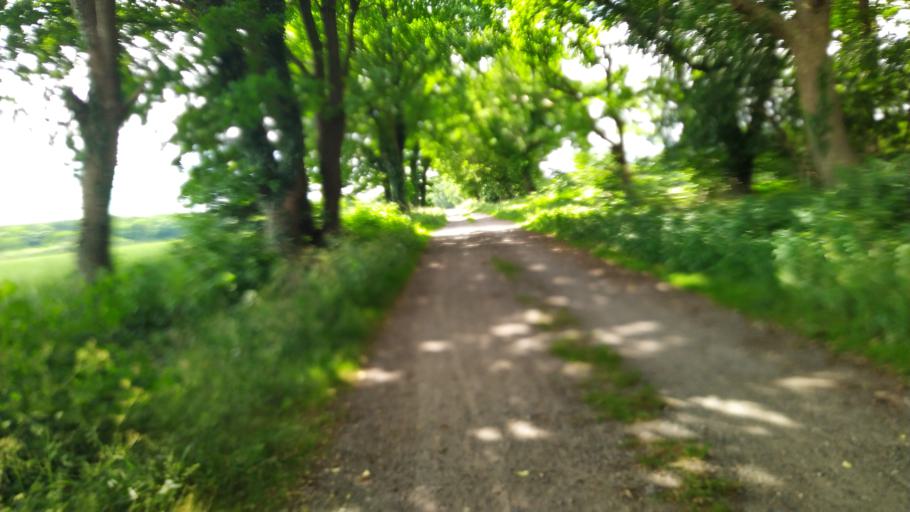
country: DE
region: Lower Saxony
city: Armstorf
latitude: 53.6035
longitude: 9.0762
